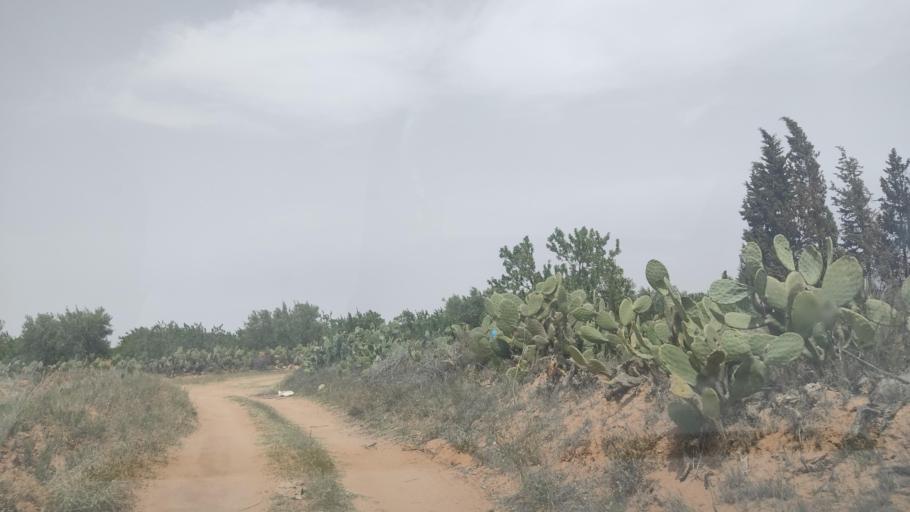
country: TN
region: Safaqis
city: Sfax
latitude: 34.8437
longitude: 10.5914
